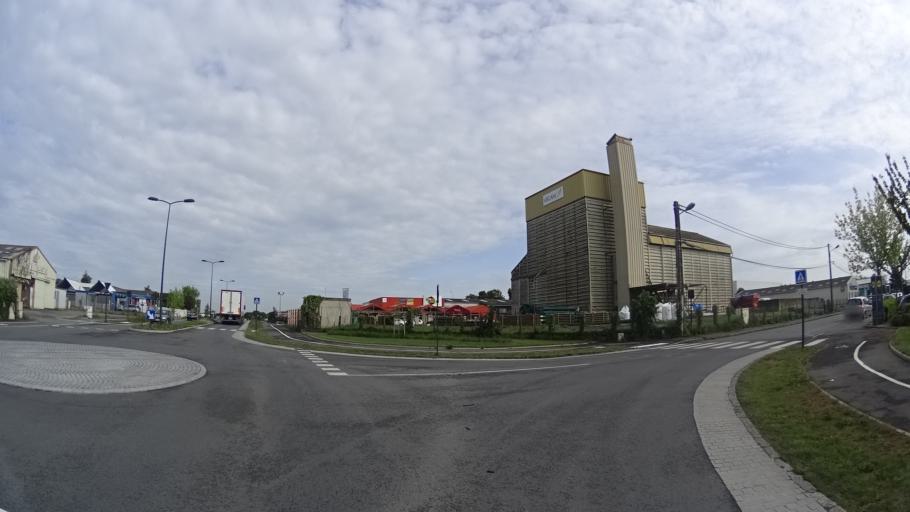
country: FR
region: Brittany
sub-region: Departement d'Ille-et-Vilaine
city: Mordelles
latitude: 48.0804
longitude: -1.8353
